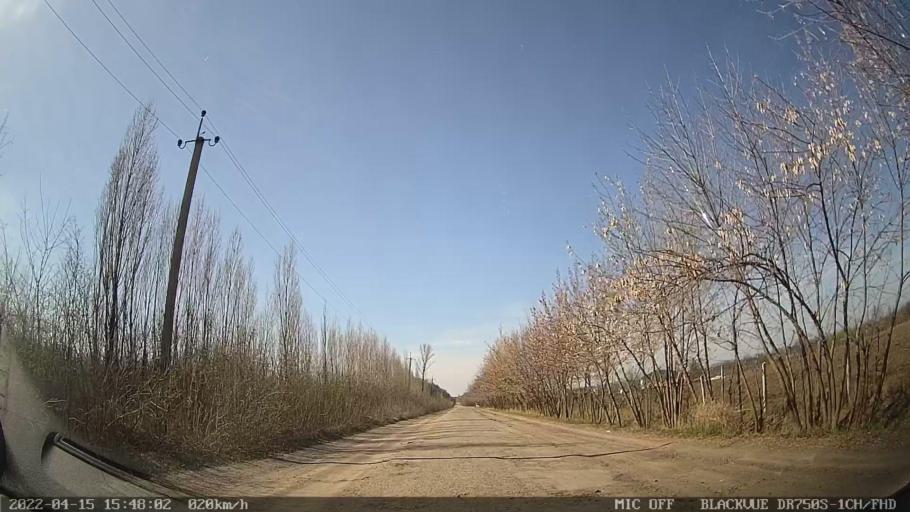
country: MD
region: Raionul Ocnita
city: Otaci
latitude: 48.3858
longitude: 27.9082
